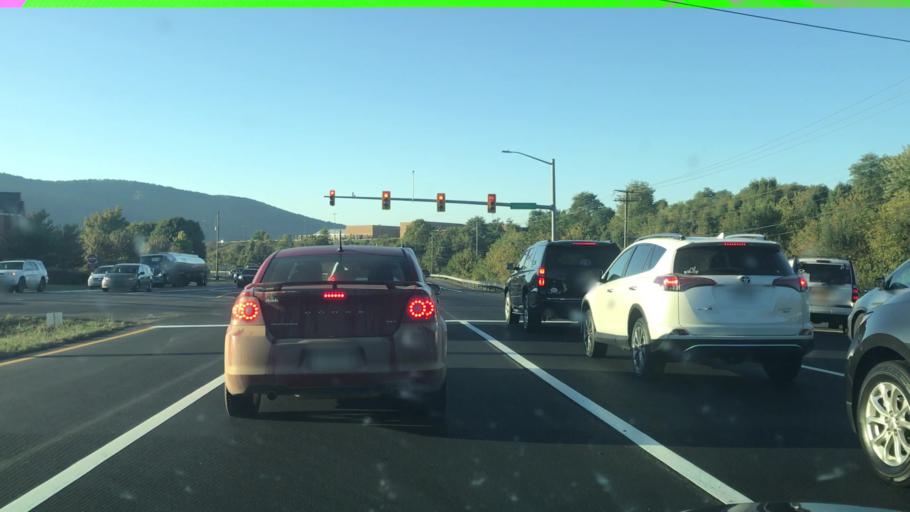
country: US
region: Virginia
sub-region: Botetourt County
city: Laymantown
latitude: 37.3300
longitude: -79.8726
